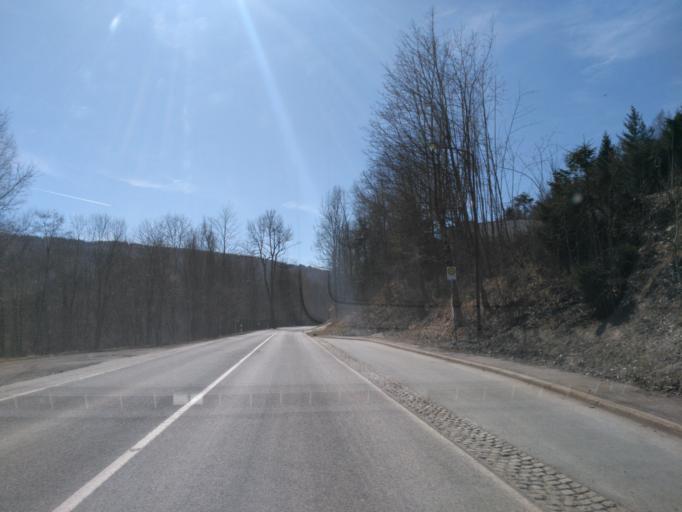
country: CZ
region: Ustecky
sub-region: Okres Chomutov
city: Vejprty
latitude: 50.4575
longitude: 13.0205
